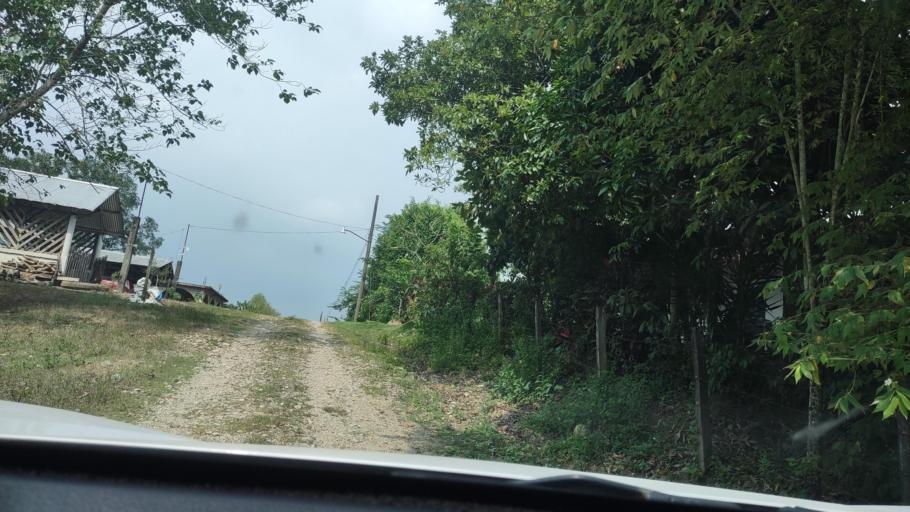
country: MX
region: Veracruz
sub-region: Uxpanapa
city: Poblado 10
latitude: 17.5454
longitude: -94.2908
